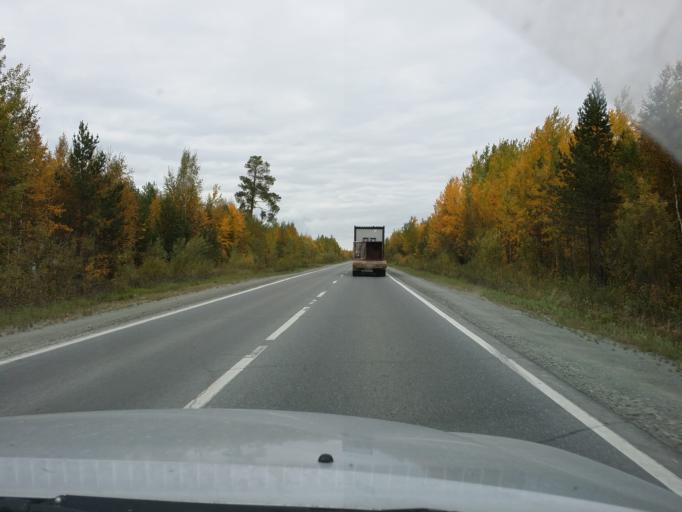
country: RU
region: Khanty-Mansiyskiy Avtonomnyy Okrug
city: Langepas
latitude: 61.1683
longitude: 75.5762
